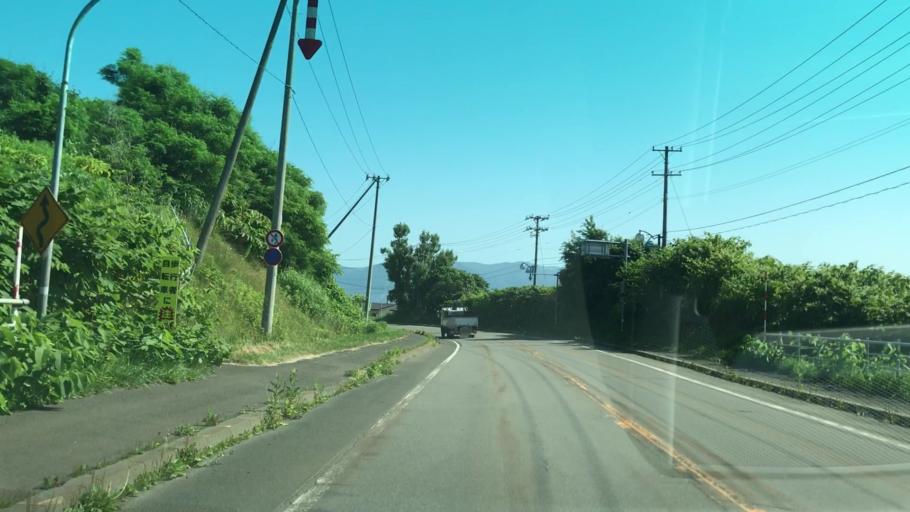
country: JP
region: Hokkaido
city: Iwanai
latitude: 43.0606
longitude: 140.4973
